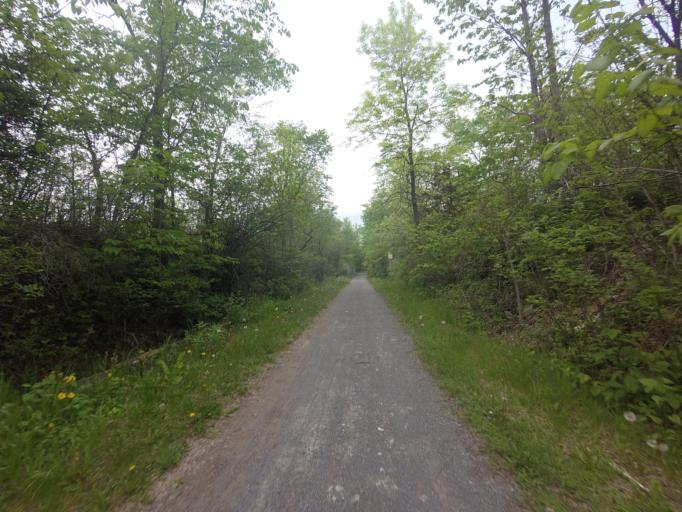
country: CA
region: Ontario
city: Kingston
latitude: 44.2966
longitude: -76.5594
